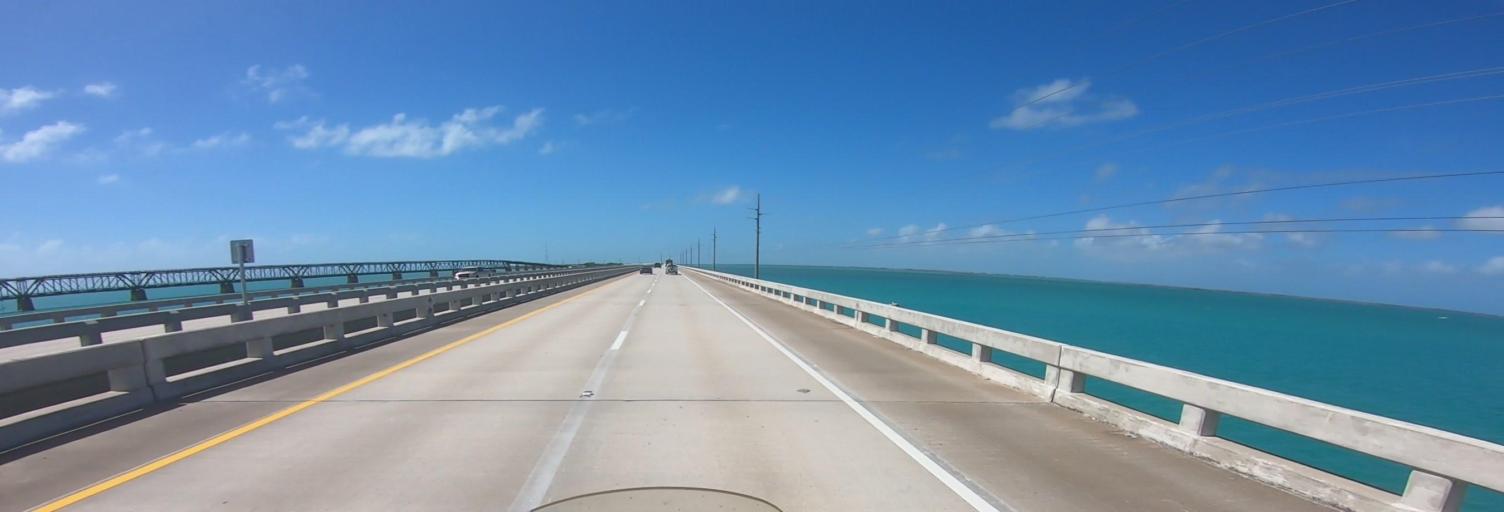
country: US
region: Florida
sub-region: Monroe County
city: Big Pine Key
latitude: 24.6583
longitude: -81.2877
